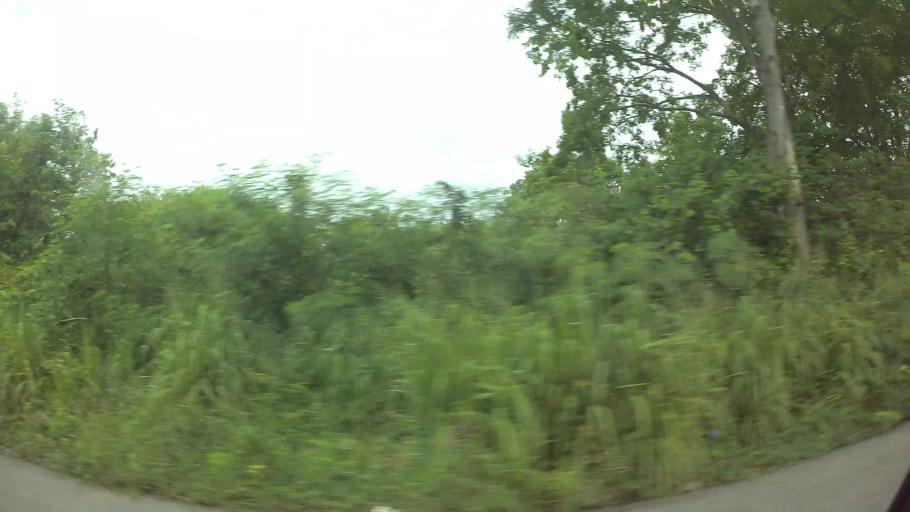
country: TH
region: Chon Buri
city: Si Racha
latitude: 13.1831
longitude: 100.9750
